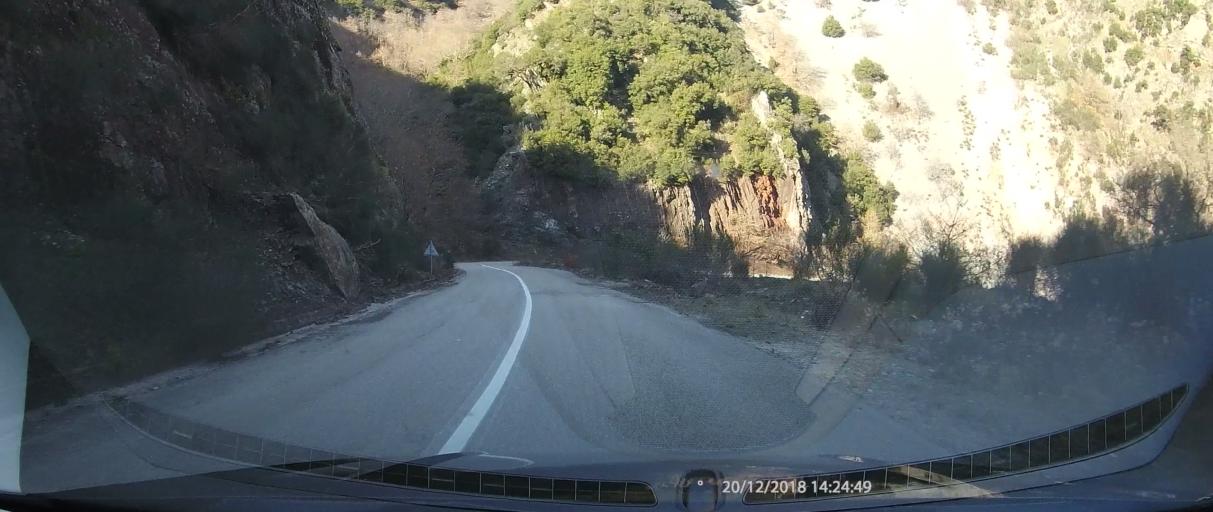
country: GR
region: West Greece
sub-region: Nomos Aitolias kai Akarnanias
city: Thermo
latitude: 38.7610
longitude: 21.6702
